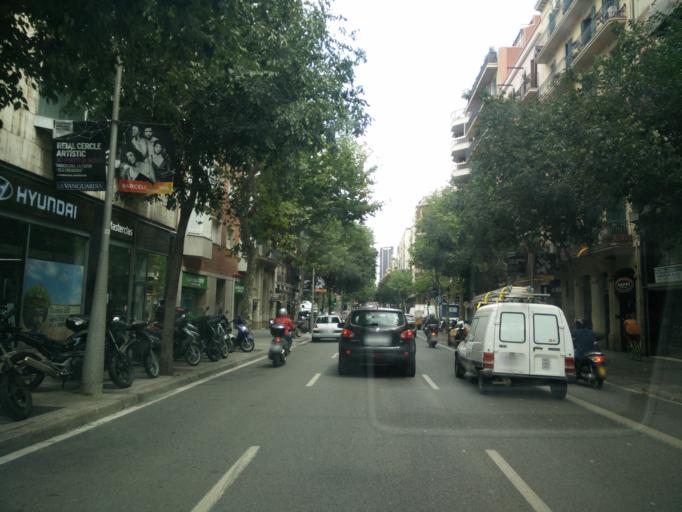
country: ES
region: Catalonia
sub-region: Provincia de Barcelona
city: Barcelona
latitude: 41.3901
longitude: 2.1486
